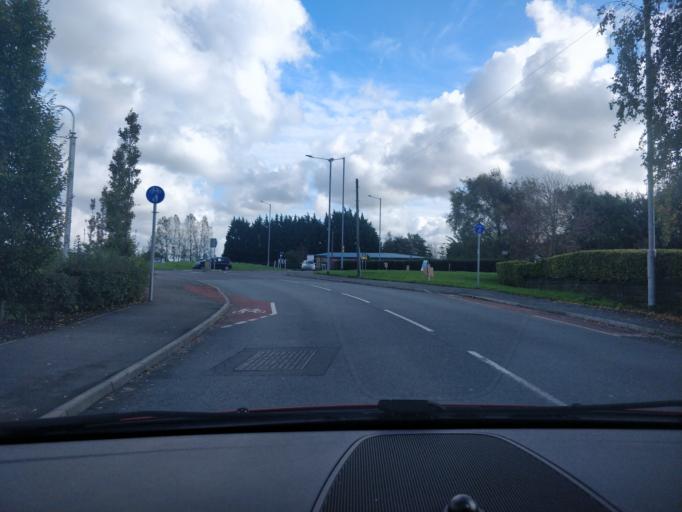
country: GB
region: England
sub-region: Lancashire
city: Ormskirk
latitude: 53.5872
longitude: -2.8647
